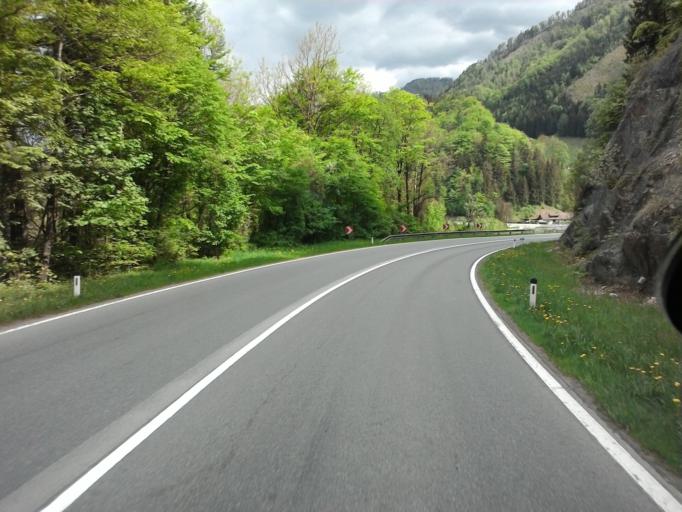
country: AT
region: Upper Austria
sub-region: Politischer Bezirk Kirchdorf an der Krems
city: Micheldorf in Oberoesterreich
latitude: 47.7738
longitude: 14.1686
